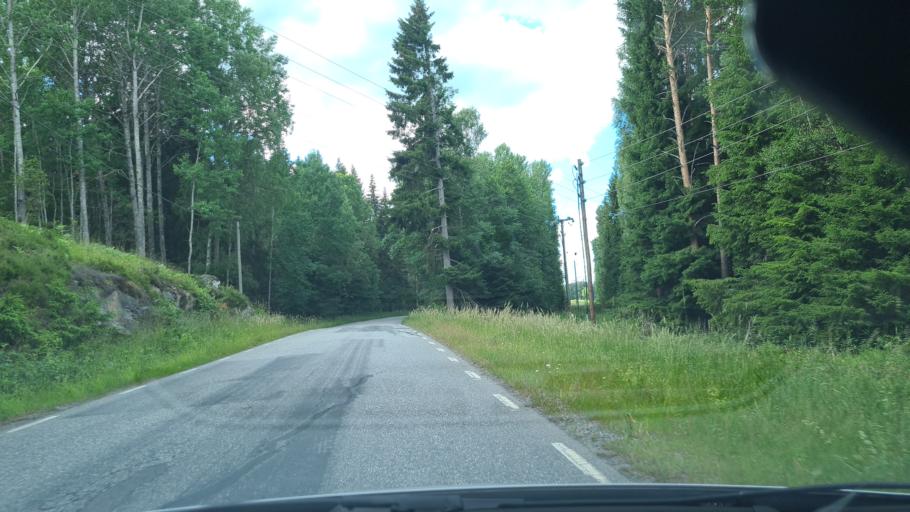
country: SE
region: Stockholm
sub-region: Varmdo Kommun
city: Mortnas
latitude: 59.4027
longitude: 18.4608
